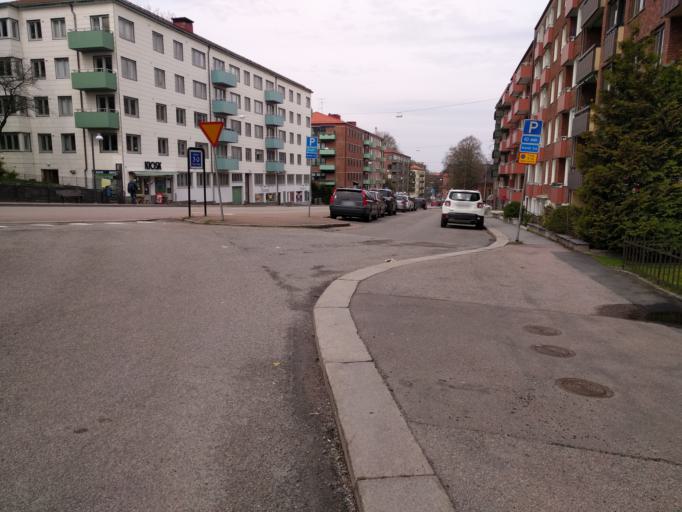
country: SE
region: Vaestra Goetaland
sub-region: Goteborg
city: Goeteborg
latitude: 57.6907
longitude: 11.9889
